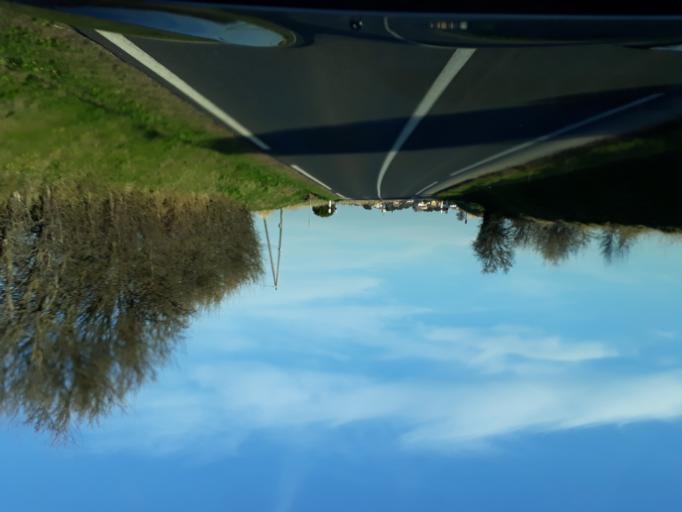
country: FR
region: Languedoc-Roussillon
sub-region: Departement de l'Herault
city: Marseillan
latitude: 43.3414
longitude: 3.5254
